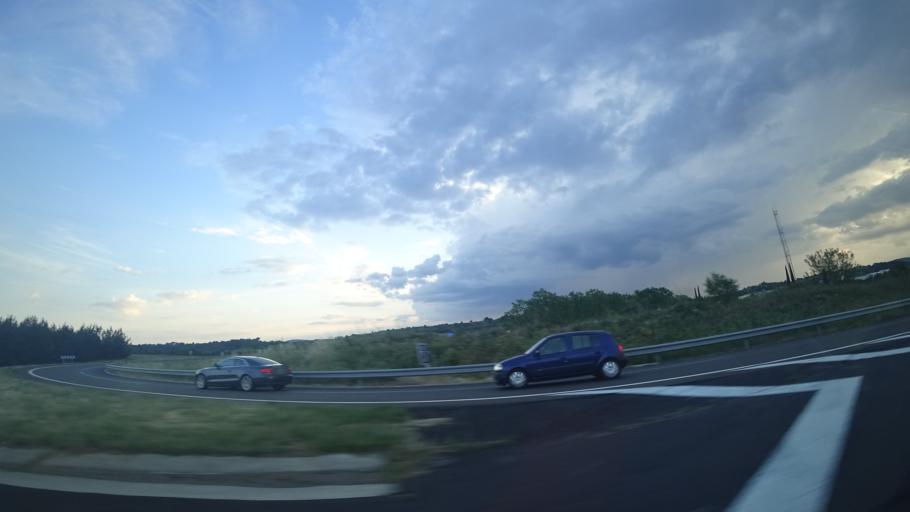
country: FR
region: Languedoc-Roussillon
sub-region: Departement de l'Herault
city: Nebian
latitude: 43.6154
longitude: 3.4599
